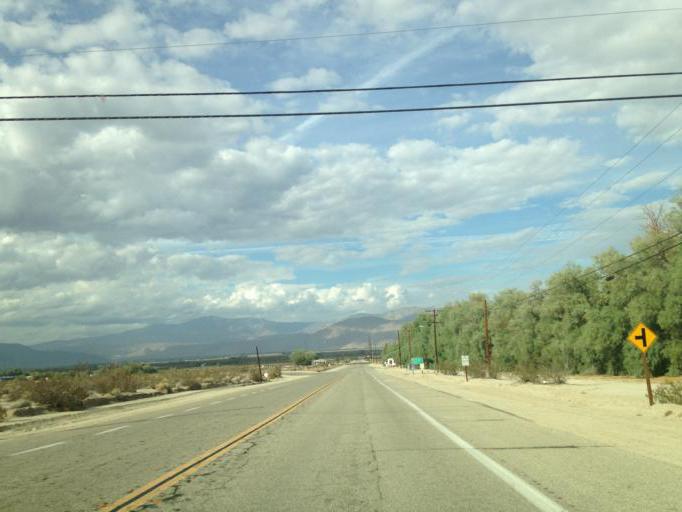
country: US
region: California
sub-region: San Diego County
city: Borrego Springs
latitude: 33.2067
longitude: -116.3300
